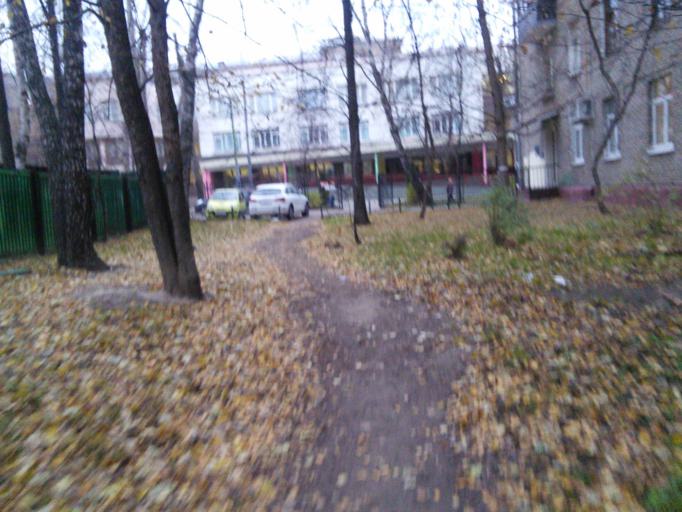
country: RU
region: Moscow
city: Likhobory
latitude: 55.8114
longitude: 37.5749
